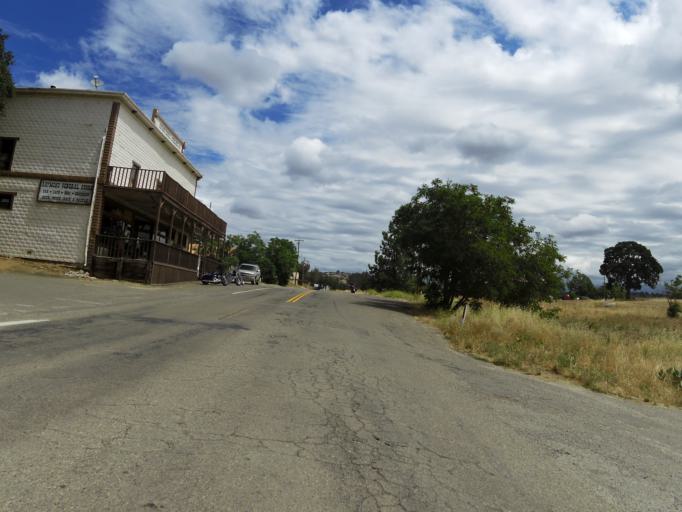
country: US
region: California
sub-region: Madera County
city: Yosemite Lakes
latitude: 37.2160
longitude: -119.9070
